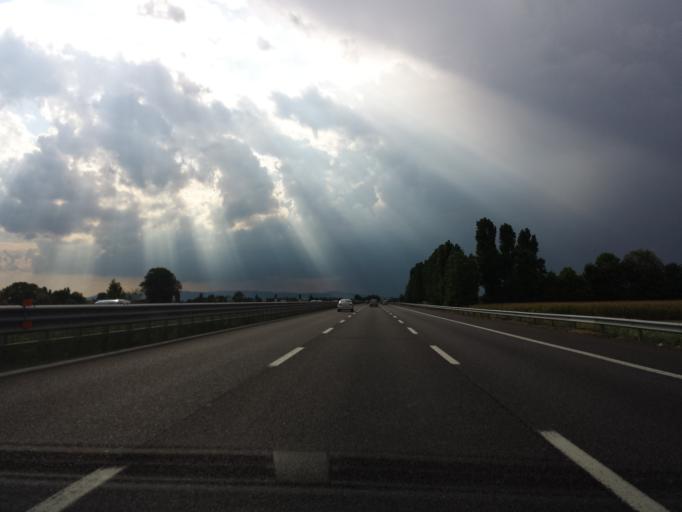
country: IT
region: Veneto
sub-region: Provincia di Padova
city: Bosco
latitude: 45.4547
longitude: 11.8020
